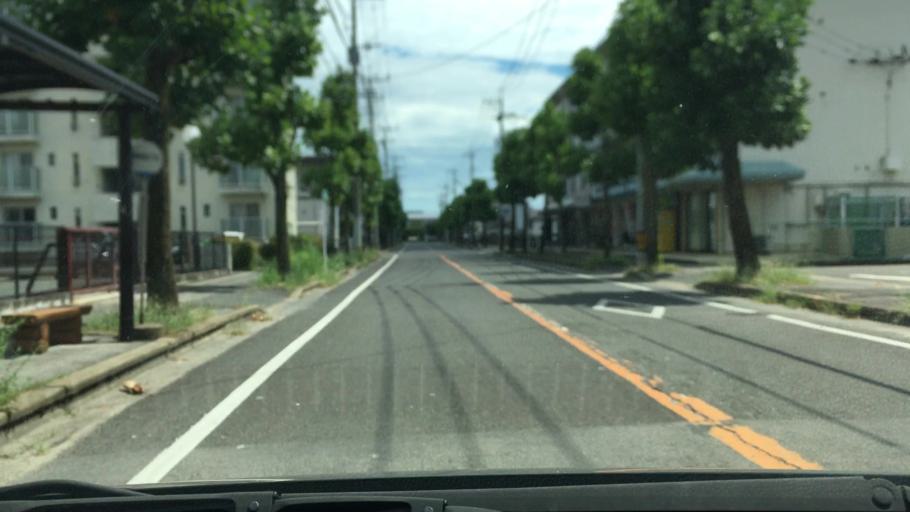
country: JP
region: Saga Prefecture
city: Saga-shi
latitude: 33.2683
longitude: 130.2871
